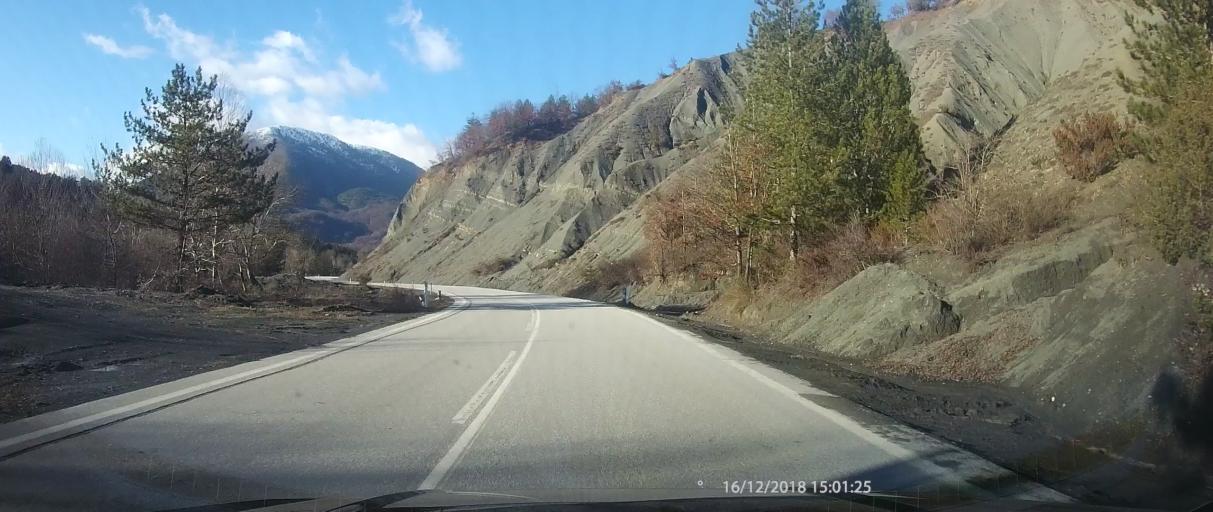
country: GR
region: West Macedonia
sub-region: Nomos Kastorias
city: Nestorio
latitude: 40.2214
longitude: 21.0065
